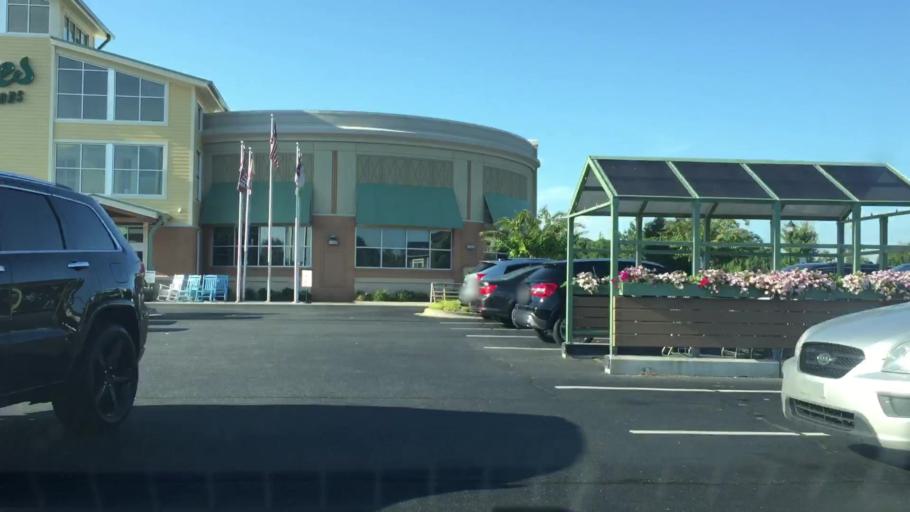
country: US
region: North Carolina
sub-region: Iredell County
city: Mooresville
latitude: 35.5870
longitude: -80.8719
